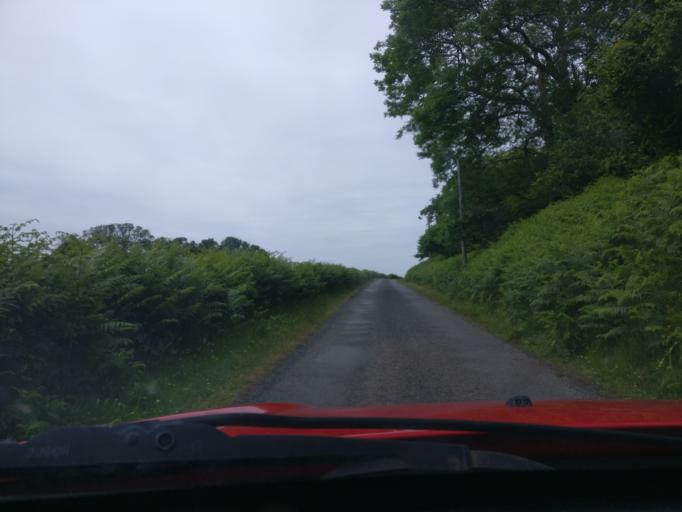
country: GB
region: Scotland
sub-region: Argyll and Bute
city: Isle Of Mull
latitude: 56.5314
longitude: -6.2266
